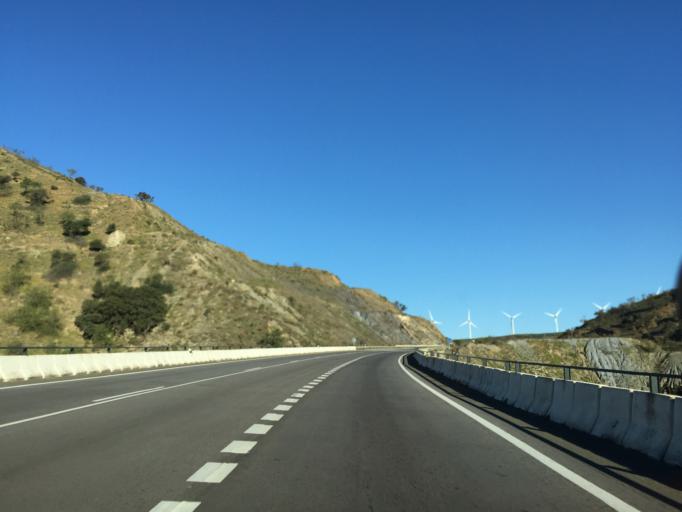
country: ES
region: Andalusia
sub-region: Provincia de Malaga
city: Carratraca
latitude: 36.8495
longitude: -4.8249
